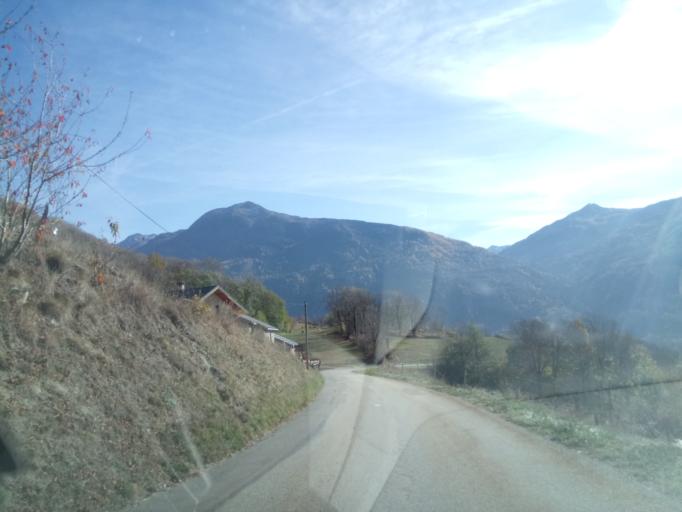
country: FR
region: Rhone-Alpes
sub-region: Departement de la Savoie
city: Saint-Michel-de-Maurienne
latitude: 45.2309
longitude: 6.4698
